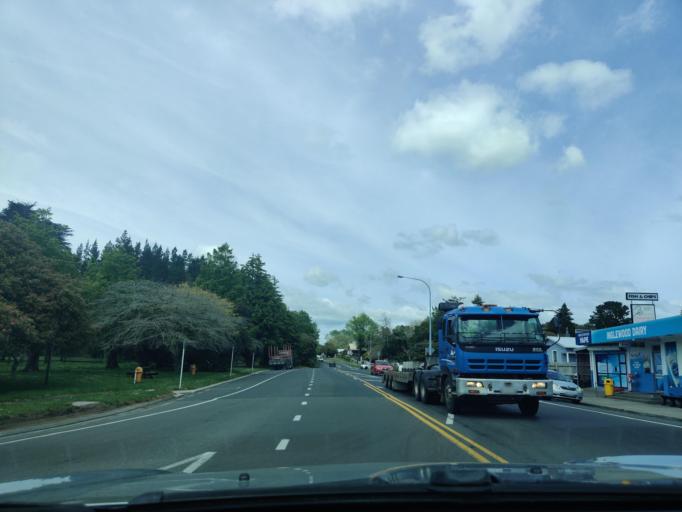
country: NZ
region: Taranaki
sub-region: New Plymouth District
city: New Plymouth
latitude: -39.1594
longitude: 174.2080
